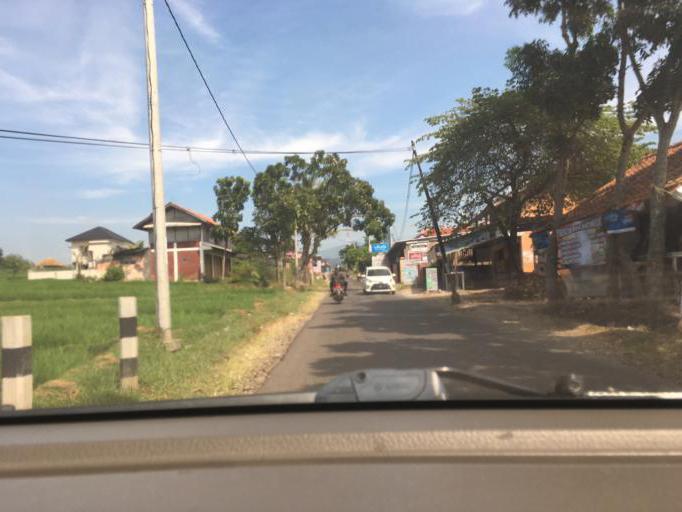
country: ID
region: West Java
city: Cilengkrang
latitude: -6.9456
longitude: 108.0996
